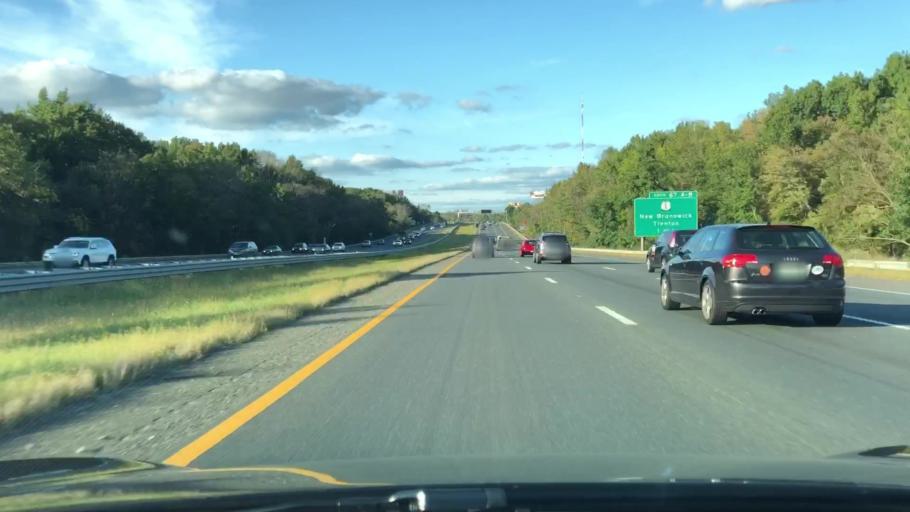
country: US
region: New Jersey
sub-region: Mercer County
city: Mercerville
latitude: 40.2655
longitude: -74.6923
